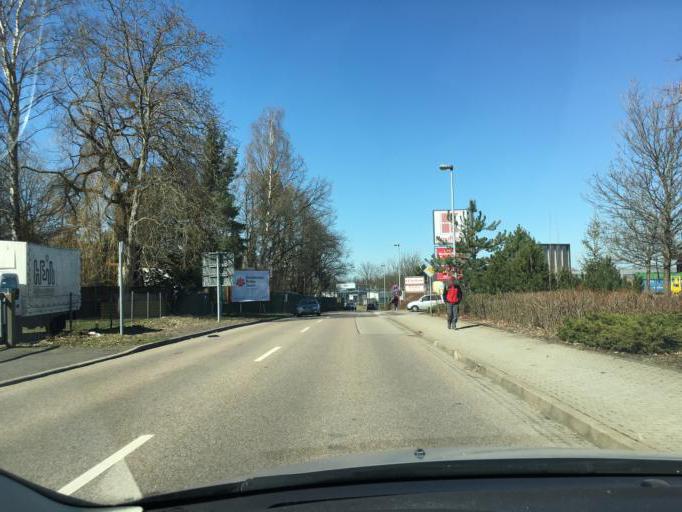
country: DE
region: Saxony
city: Limbach-Oberfrohna
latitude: 50.8547
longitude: 12.7837
